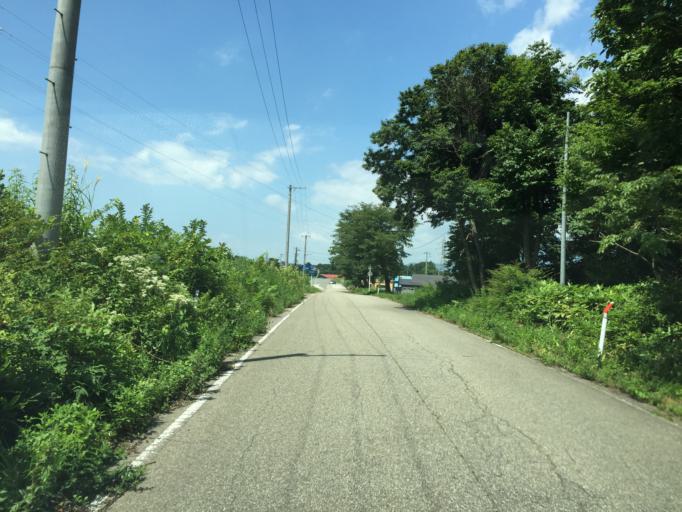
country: JP
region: Fukushima
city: Inawashiro
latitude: 37.5047
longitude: 140.0162
